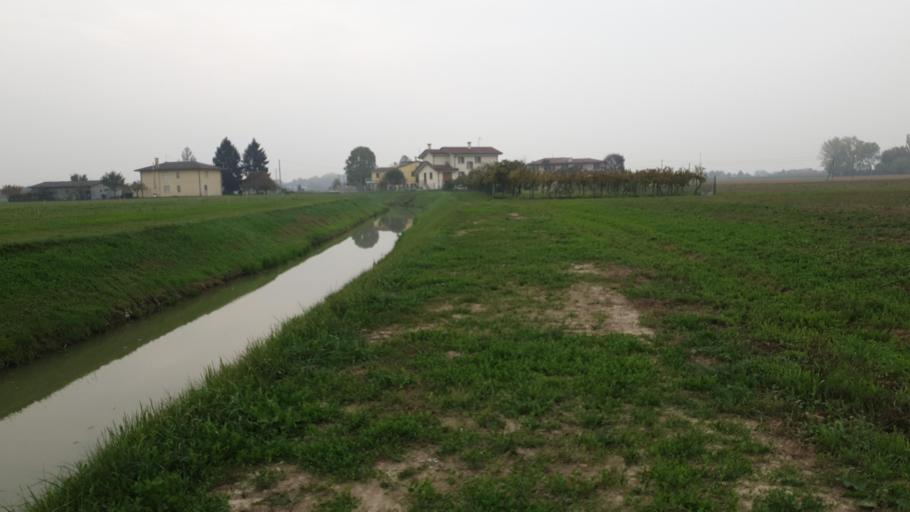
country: IT
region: Veneto
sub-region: Provincia di Padova
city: Casalserugo
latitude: 45.3095
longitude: 11.9248
